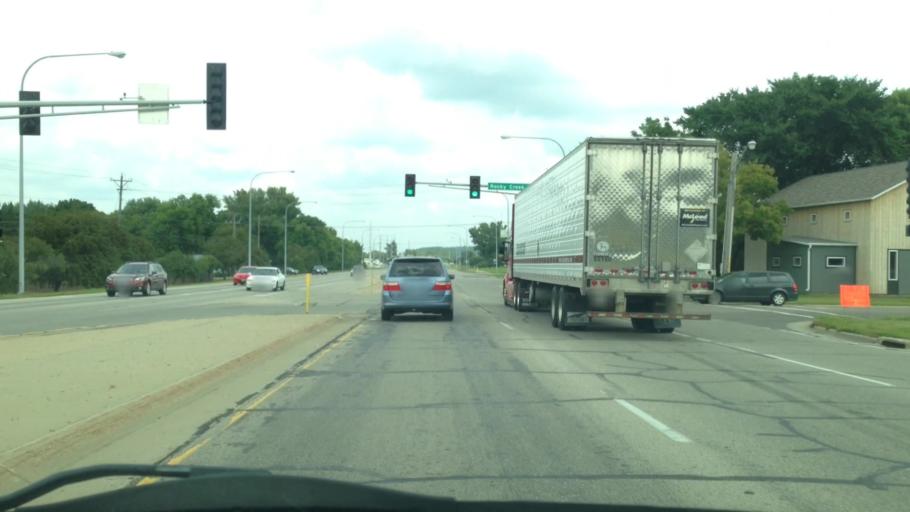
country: US
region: Minnesota
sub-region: Olmsted County
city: Rochester
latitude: 44.0542
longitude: -92.4547
